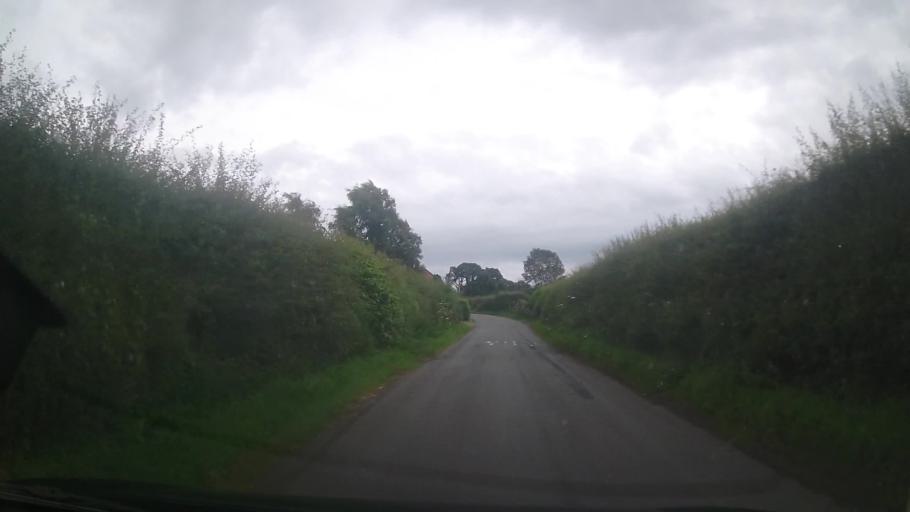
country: GB
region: England
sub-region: Shropshire
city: Wem
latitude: 52.9065
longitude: -2.7296
